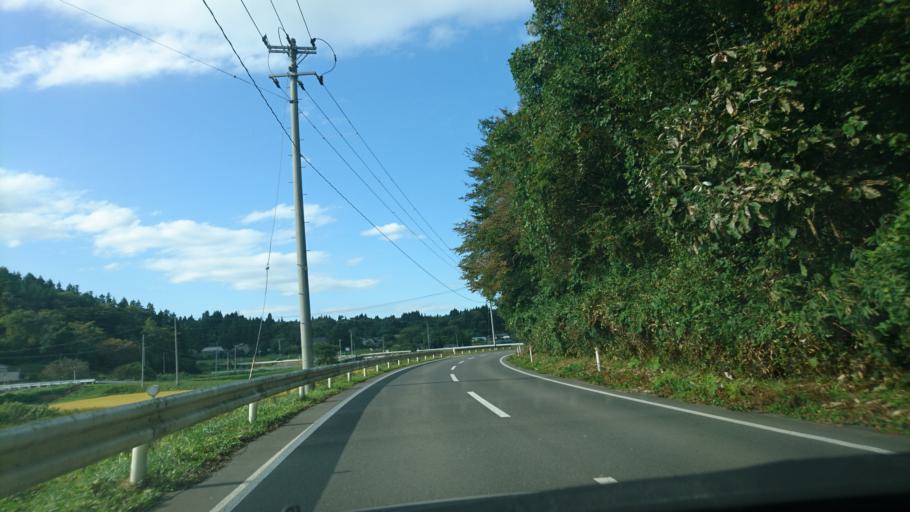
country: JP
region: Iwate
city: Ichinoseki
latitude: 38.8754
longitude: 141.3431
